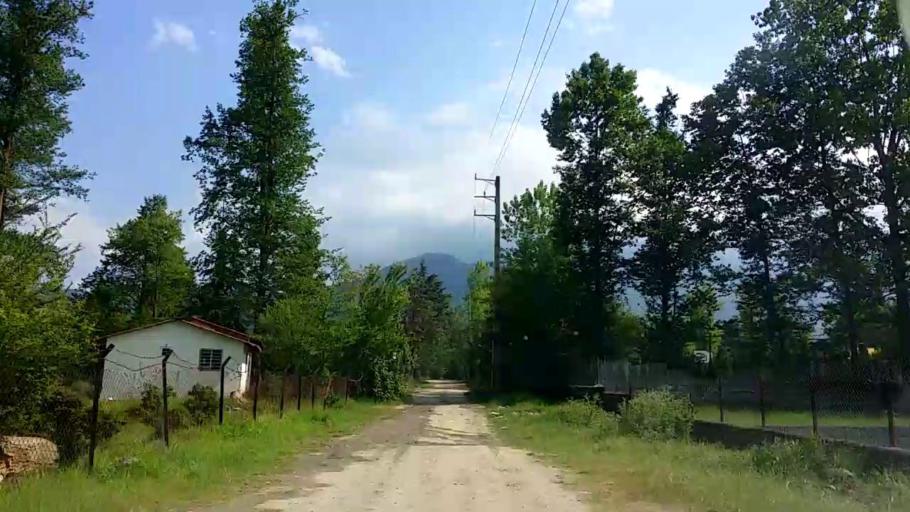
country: IR
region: Mazandaran
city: `Abbasabad
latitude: 36.5263
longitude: 51.1828
